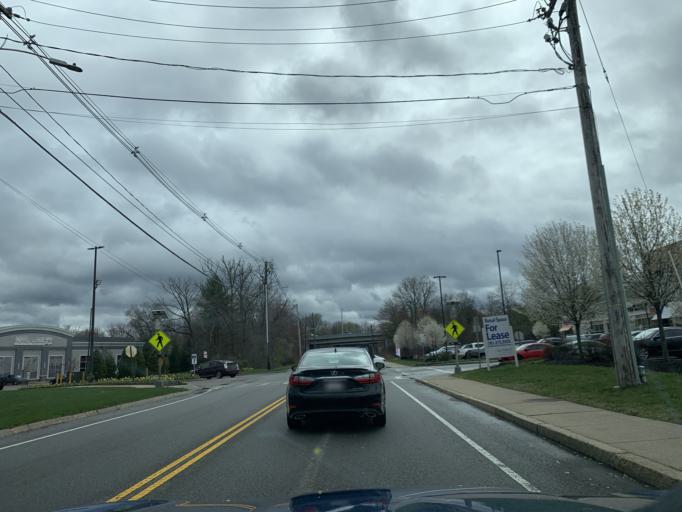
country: US
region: Massachusetts
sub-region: Bristol County
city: Mansfield Center
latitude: 42.0140
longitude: -71.2321
